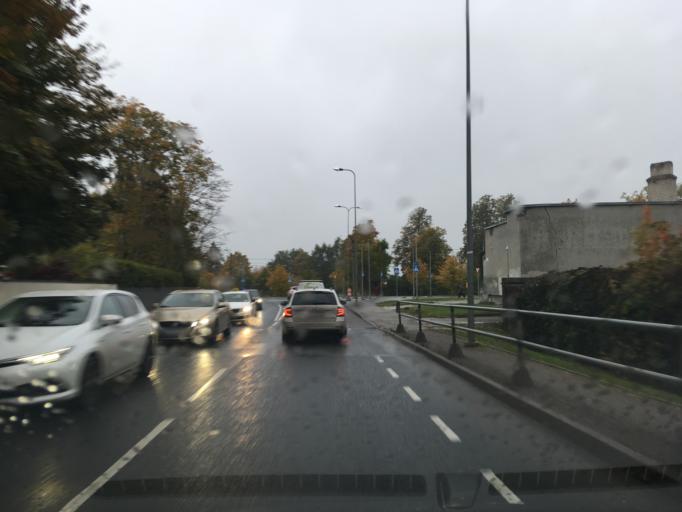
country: EE
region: Harju
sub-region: Tallinna linn
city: Kose
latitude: 59.4575
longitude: 24.8628
